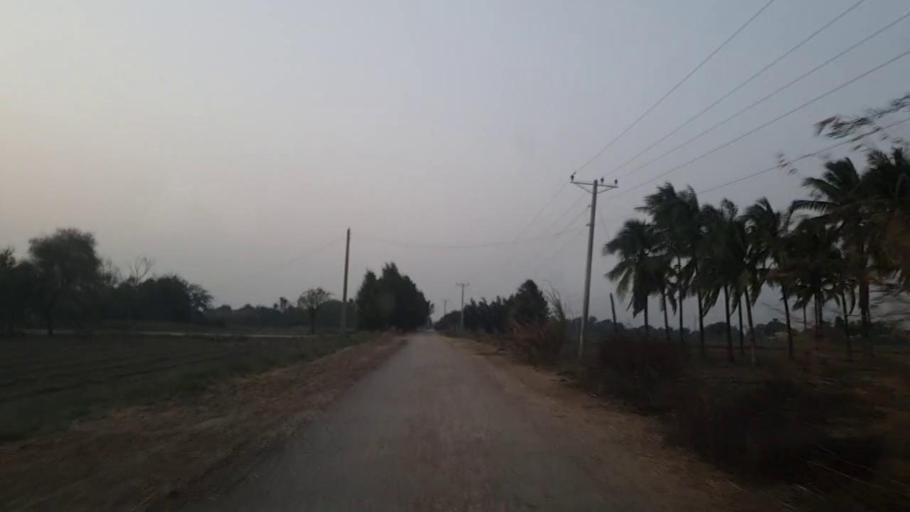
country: PK
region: Sindh
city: Mirpur Sakro
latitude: 24.5914
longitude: 67.7799
